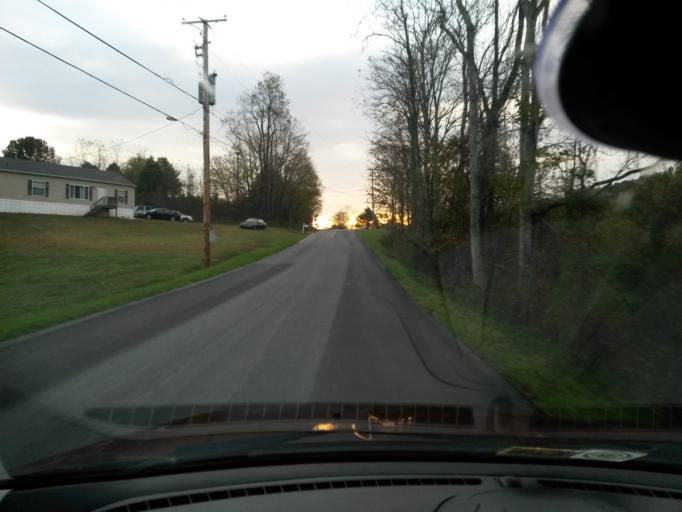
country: US
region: Virginia
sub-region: Roanoke County
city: Narrows
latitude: 37.1668
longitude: -79.8703
